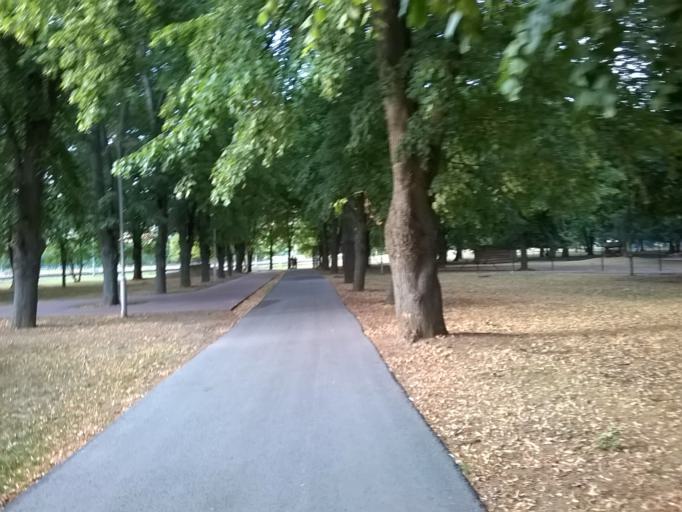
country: SK
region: Nitriansky
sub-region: Okres Nitra
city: Nitra
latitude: 48.3223
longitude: 18.0848
